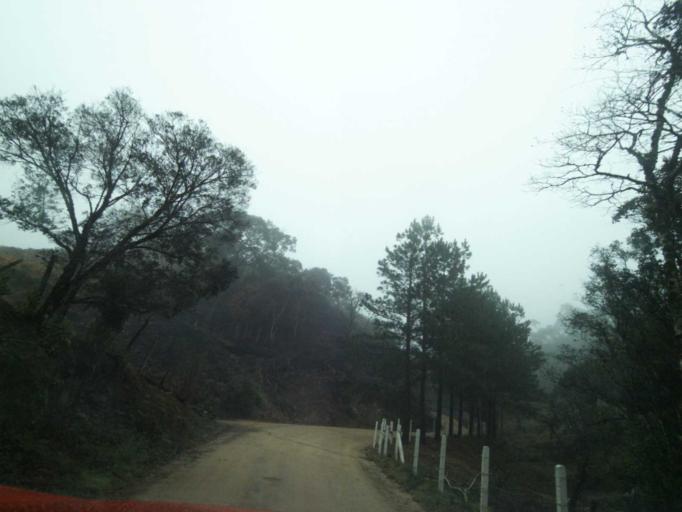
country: BR
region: Santa Catarina
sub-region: Anitapolis
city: Anitapolis
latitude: -27.9018
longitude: -49.1608
